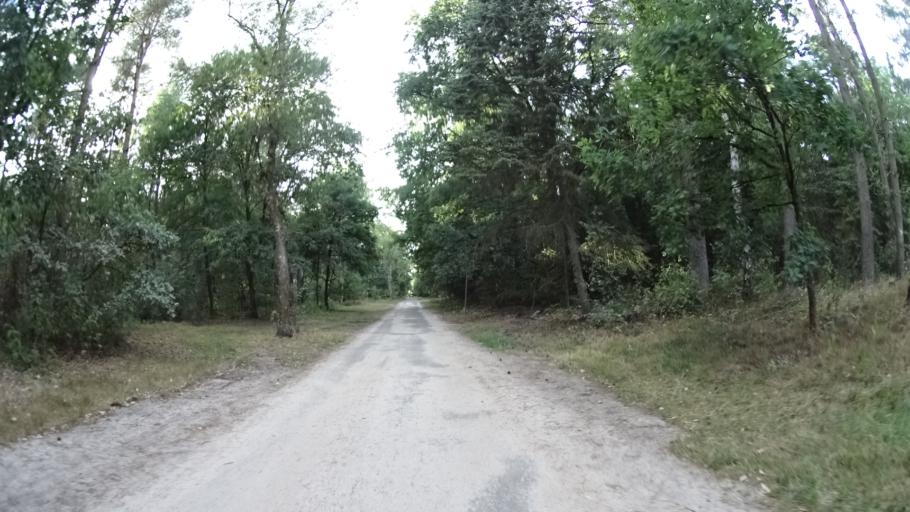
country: DE
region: Lower Saxony
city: Handeloh
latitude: 53.2337
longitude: 9.8678
